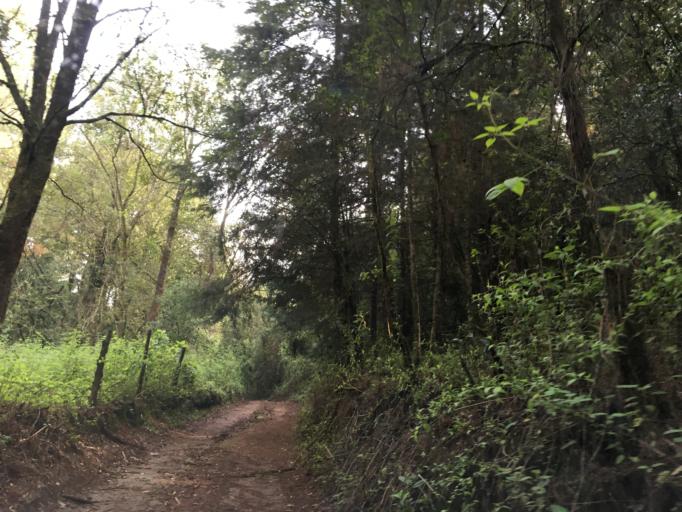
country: MX
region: Michoacan
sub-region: Zitacuaro
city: Francisco Serrato (San Bartolo)
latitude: 19.5052
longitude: -100.3063
